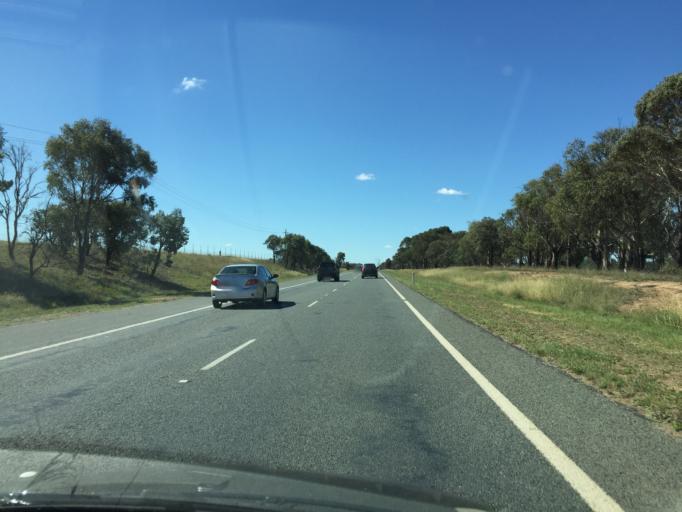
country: AU
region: Australian Capital Territory
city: Macarthur
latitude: -35.3789
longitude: 149.1696
